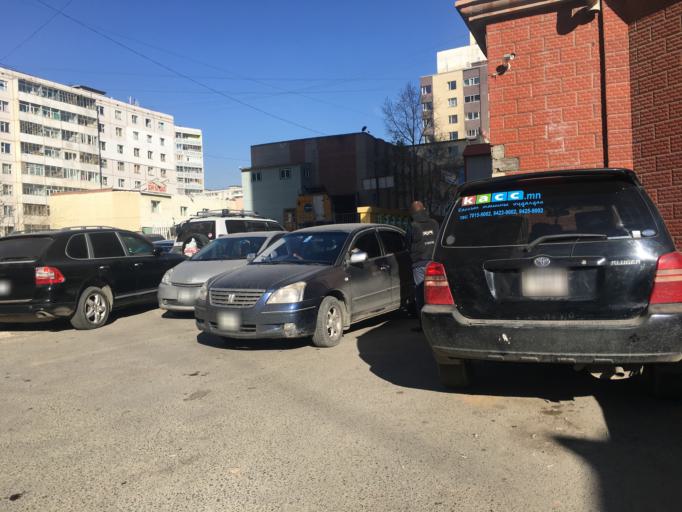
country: MN
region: Ulaanbaatar
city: Ulaanbaatar
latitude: 47.9214
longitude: 106.8894
